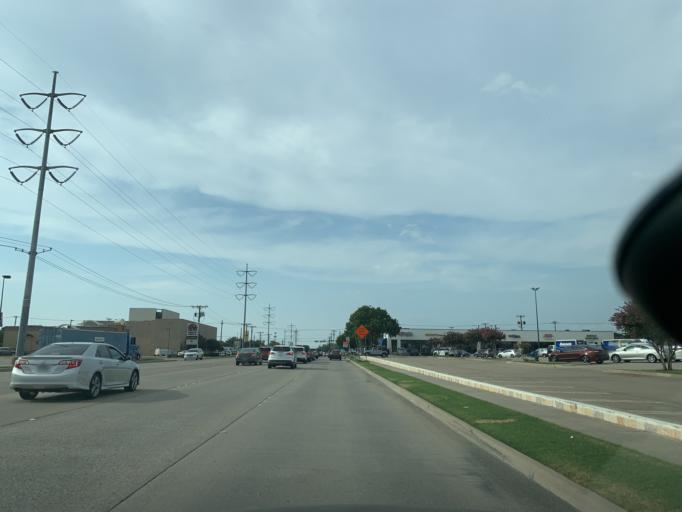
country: US
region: Texas
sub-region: Tarrant County
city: Watauga
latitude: 32.8582
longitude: -97.2380
